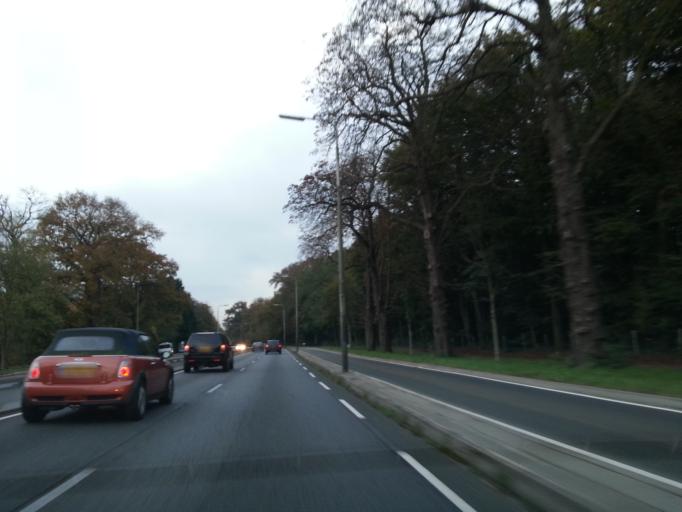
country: NL
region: South Holland
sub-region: Gemeente Wassenaar
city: Wassenaar
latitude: 52.1234
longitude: 4.3859
